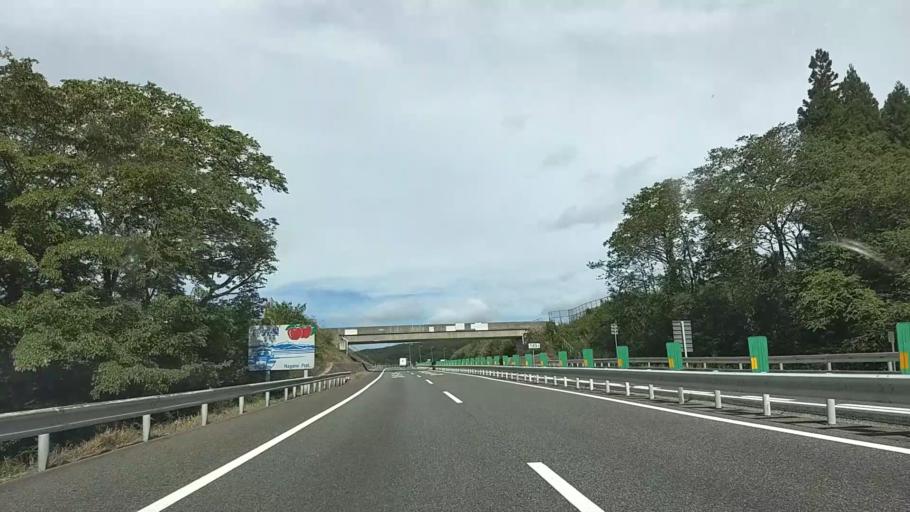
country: JP
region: Nagano
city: Chino
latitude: 35.8787
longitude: 138.3034
